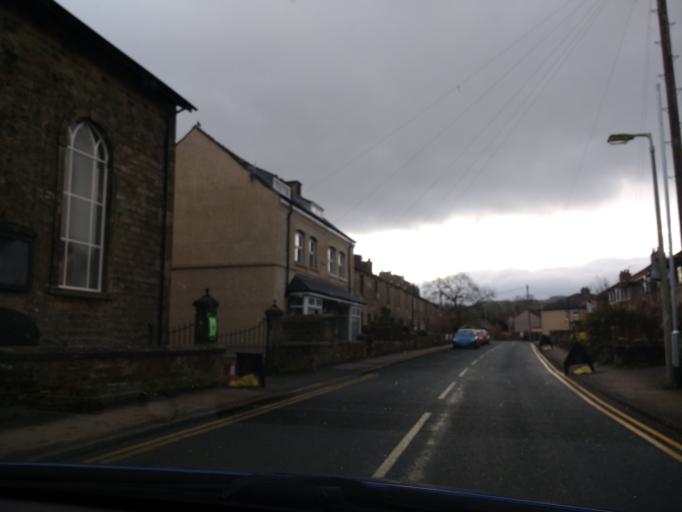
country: GB
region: England
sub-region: Lancashire
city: Caton
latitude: 54.0752
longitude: -2.7172
